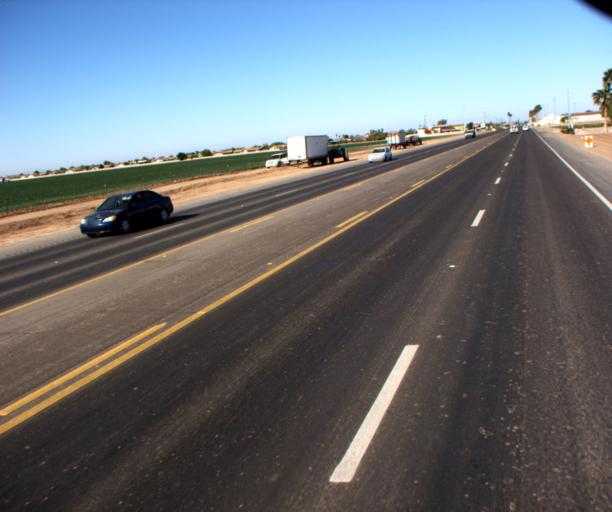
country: US
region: Arizona
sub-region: Yuma County
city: Somerton
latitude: 32.5968
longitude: -114.6972
